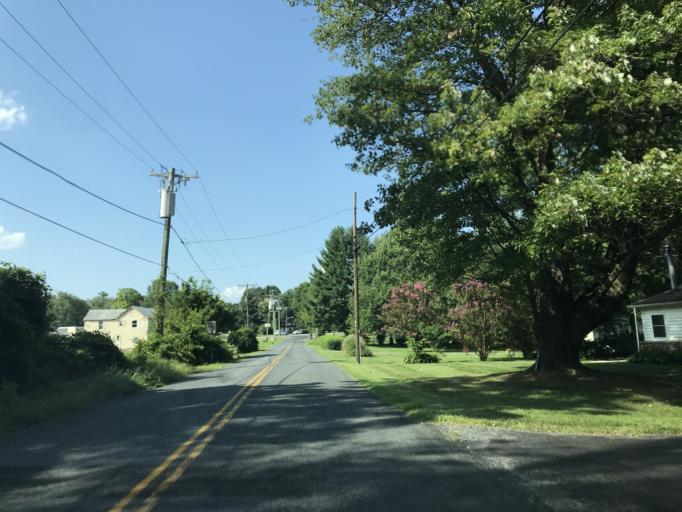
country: US
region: Maryland
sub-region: Harford County
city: South Bel Air
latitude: 39.6295
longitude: -76.2743
